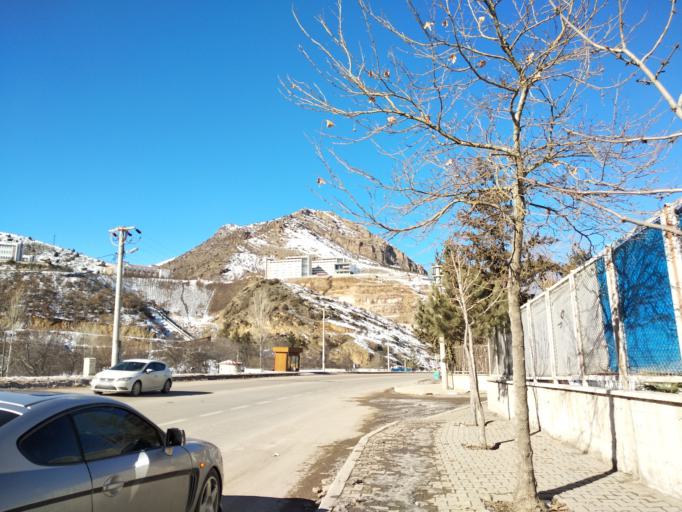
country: TR
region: Gumushane
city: Gumushkhane
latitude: 40.4375
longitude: 39.5061
